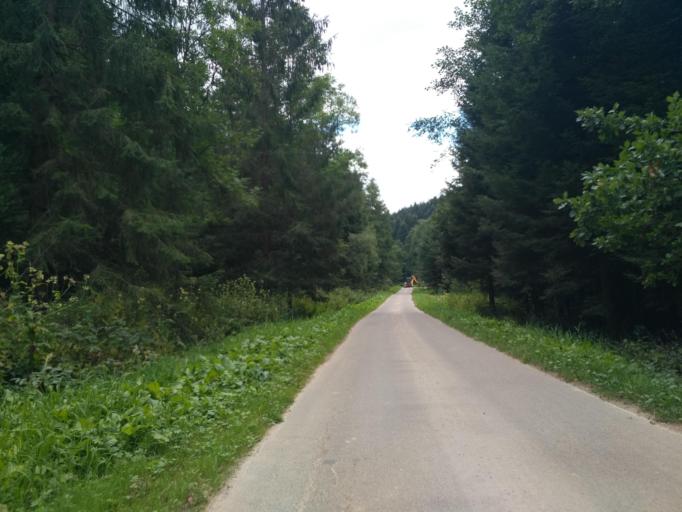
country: PL
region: Subcarpathian Voivodeship
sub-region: Powiat rzeszowski
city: Dynow
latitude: 49.7556
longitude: 22.2911
